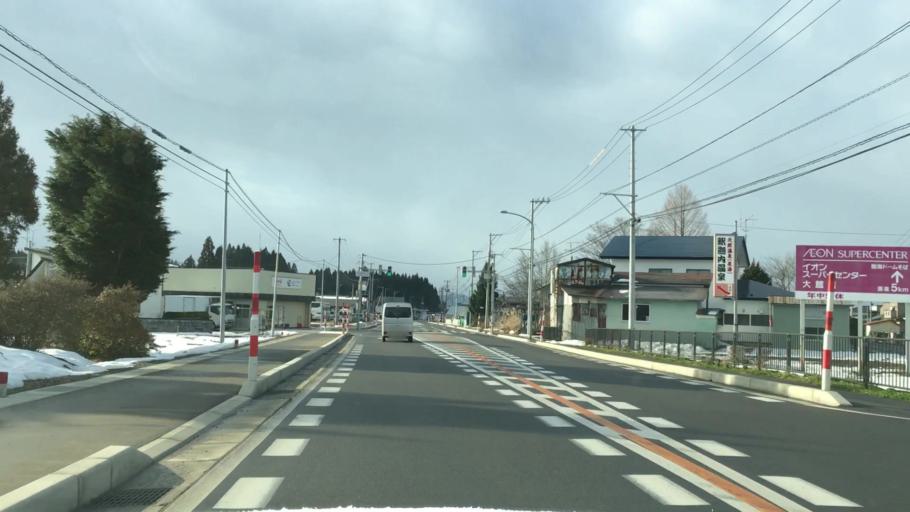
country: JP
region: Akita
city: Odate
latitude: 40.3107
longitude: 140.5703
